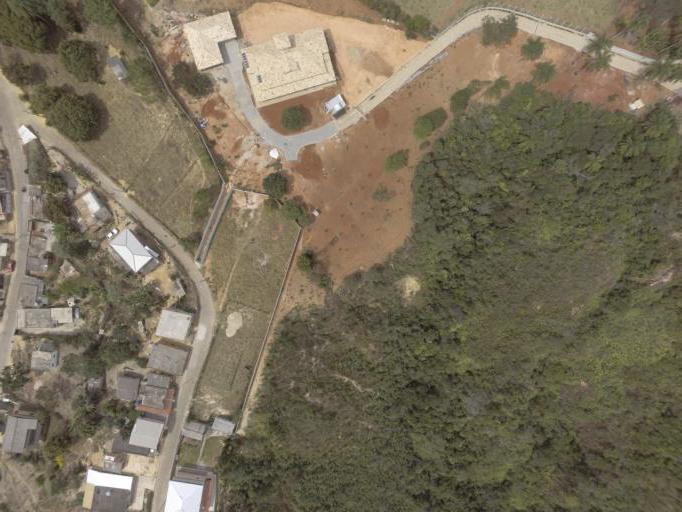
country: BR
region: Minas Gerais
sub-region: Tiradentes
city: Tiradentes
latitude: -21.0570
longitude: -44.0715
